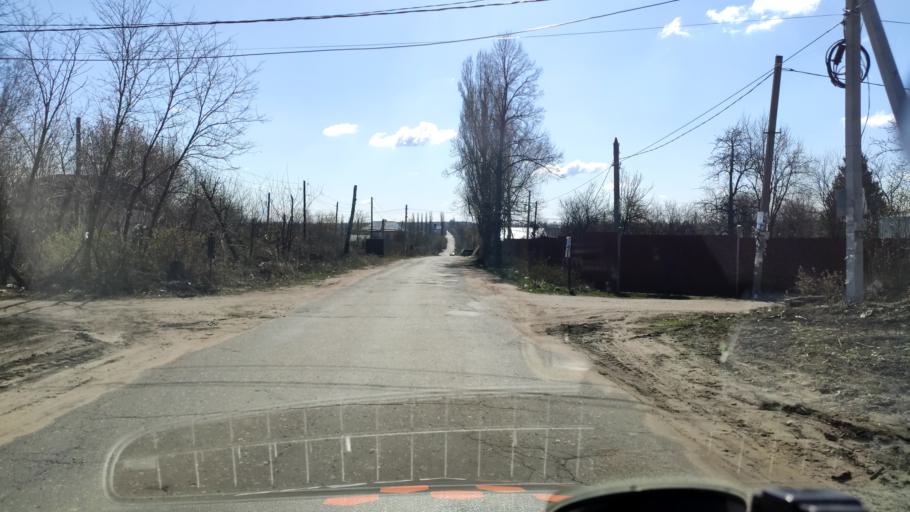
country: RU
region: Voronezj
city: Shilovo
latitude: 51.5979
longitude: 39.1477
